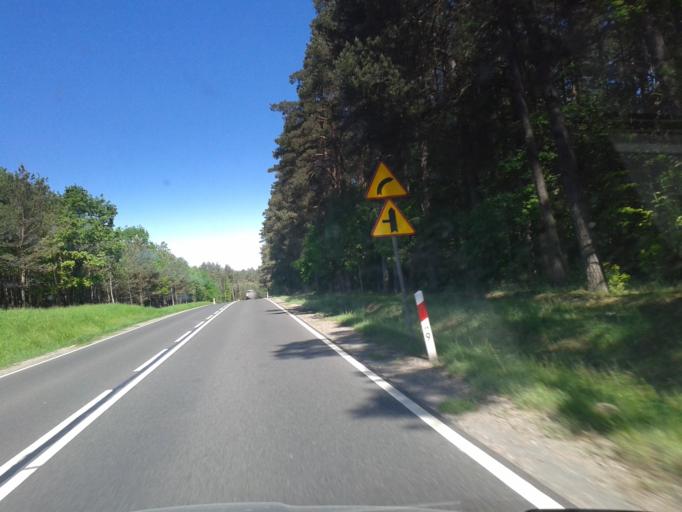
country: PL
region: West Pomeranian Voivodeship
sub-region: Powiat koszalinski
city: Sianow
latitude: 54.0648
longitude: 16.4052
